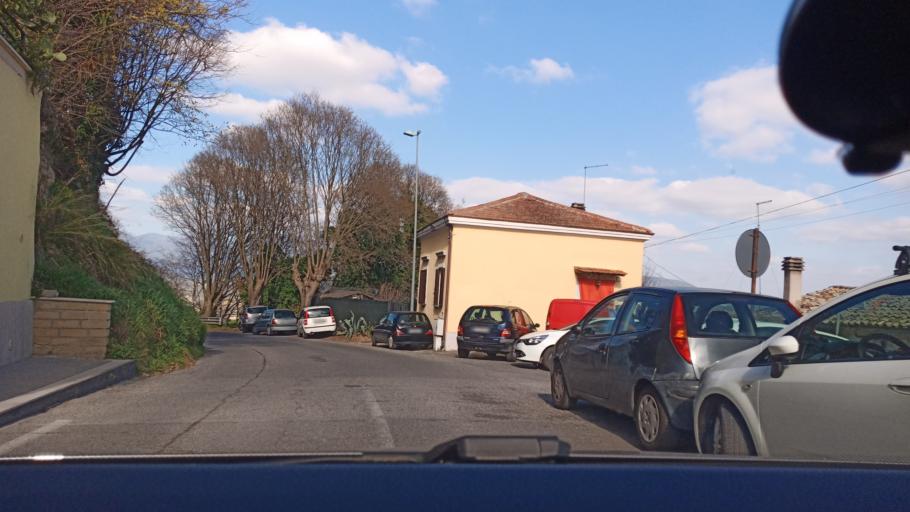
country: IT
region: Latium
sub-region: Citta metropolitana di Roma Capitale
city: Torrita Tiberina
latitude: 42.2370
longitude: 12.6182
